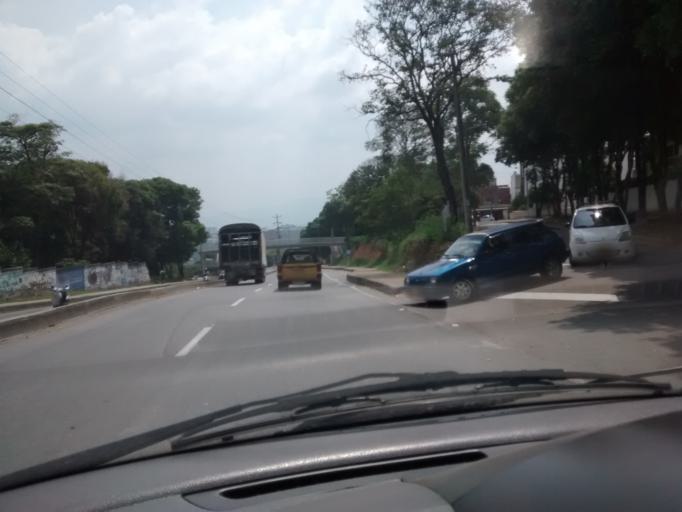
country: CO
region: Santander
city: Bucaramanga
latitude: 7.0996
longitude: -73.1134
